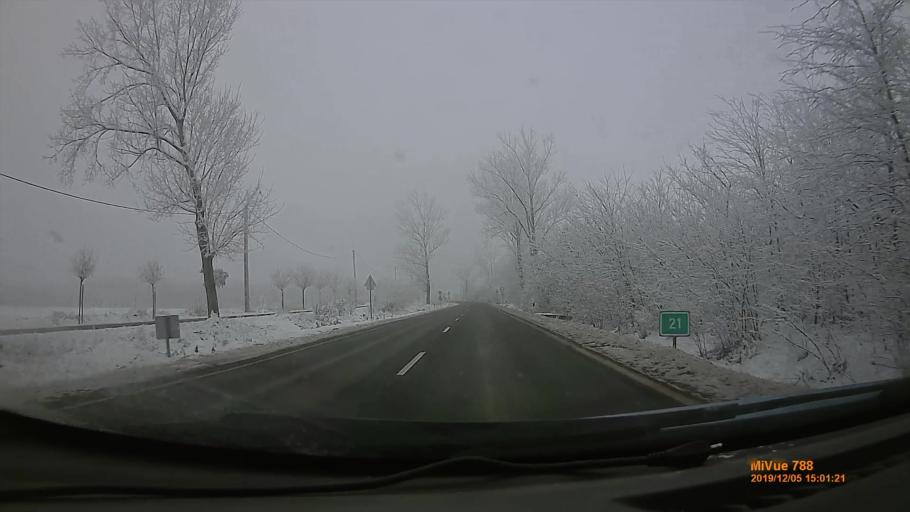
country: HU
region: Szabolcs-Szatmar-Bereg
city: Tiszanagyfalu
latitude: 48.0680
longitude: 21.5287
